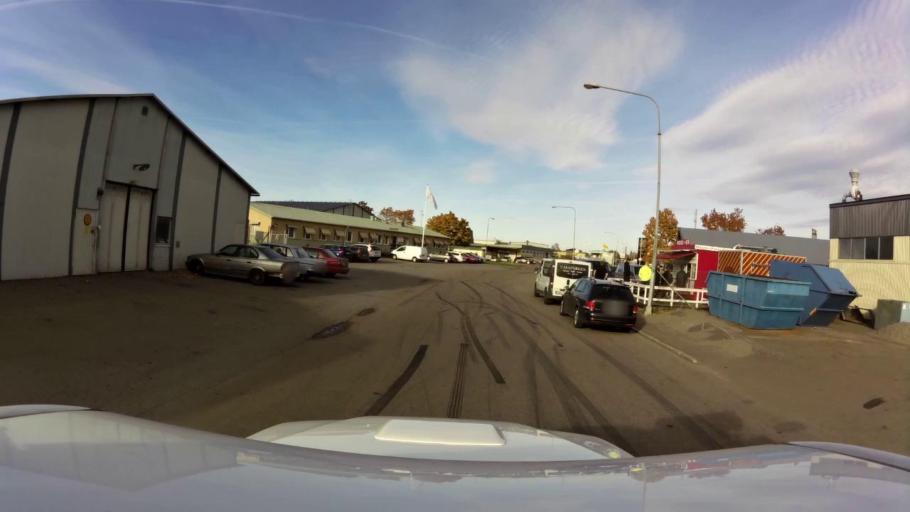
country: SE
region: OEstergoetland
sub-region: Linkopings Kommun
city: Linkoping
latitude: 58.4265
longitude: 15.6173
